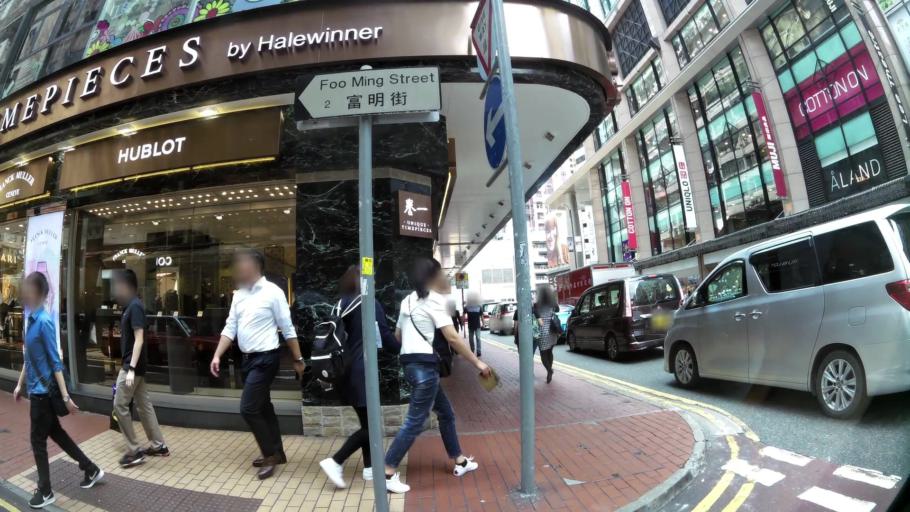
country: HK
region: Wanchai
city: Wan Chai
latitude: 22.2787
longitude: 114.1840
